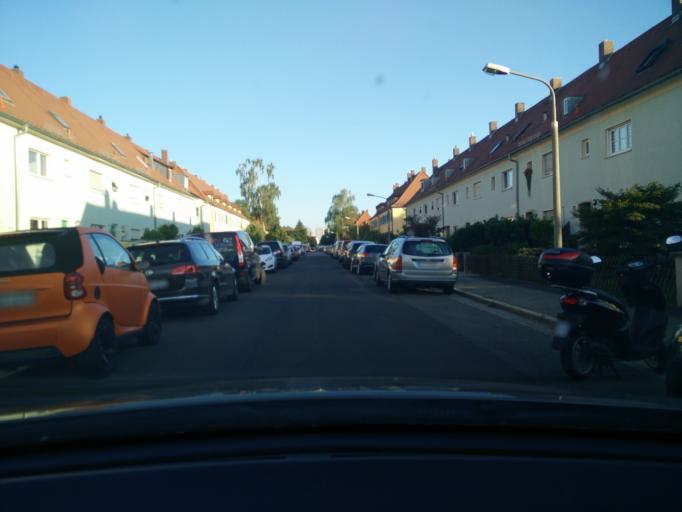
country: DE
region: Bavaria
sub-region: Regierungsbezirk Mittelfranken
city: Nuernberg
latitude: 49.4111
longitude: 11.0805
